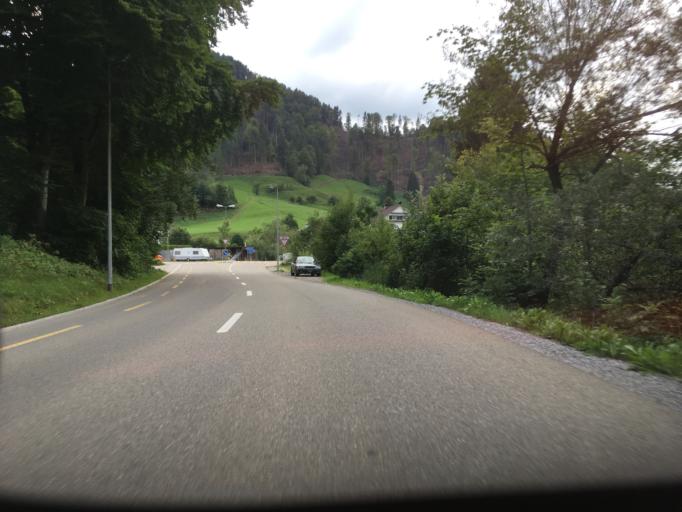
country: CH
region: Zurich
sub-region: Bezirk Pfaeffikon
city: Bauma
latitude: 47.3502
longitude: 8.9364
